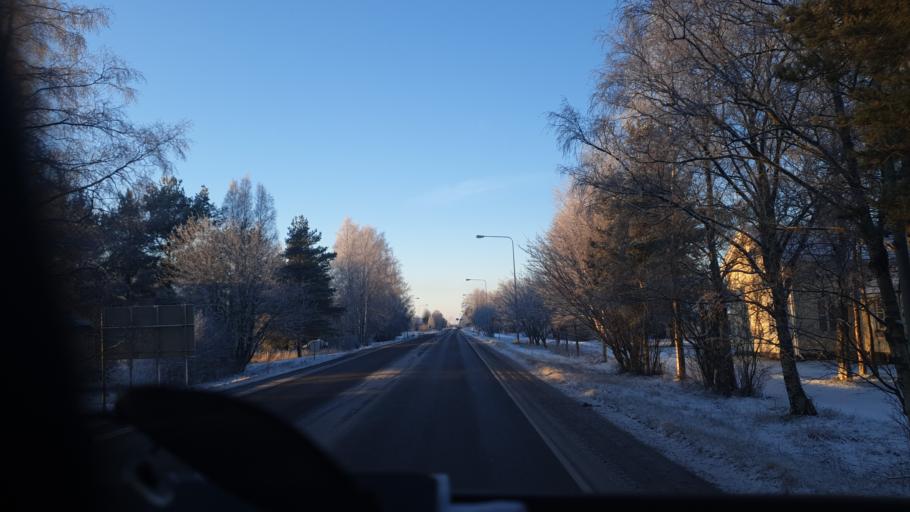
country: FI
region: Northern Ostrobothnia
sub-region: Ylivieska
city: Kalajoki
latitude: 64.2544
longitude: 23.9327
